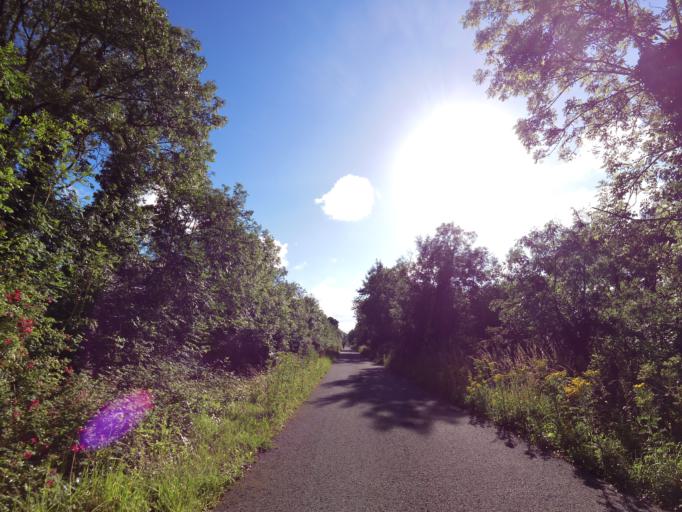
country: IE
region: Leinster
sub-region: An Iarmhi
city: Moate
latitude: 53.4036
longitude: -7.6895
